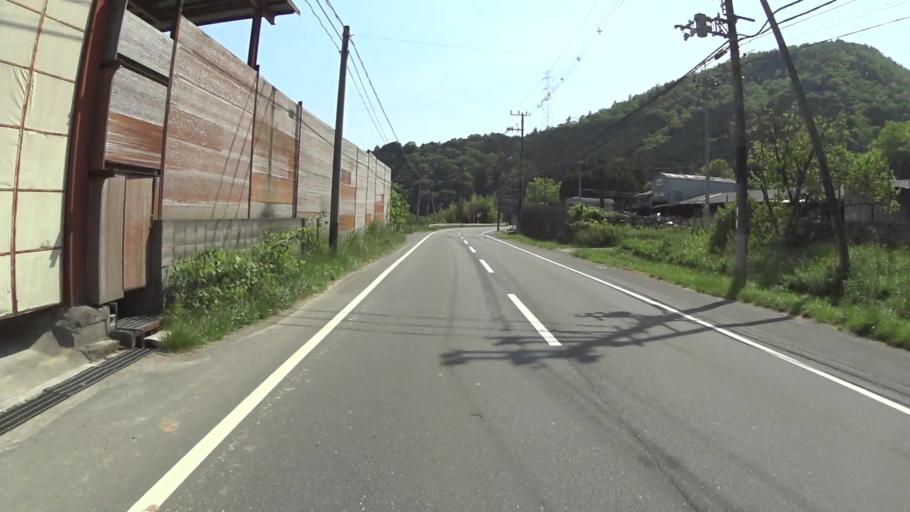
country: JP
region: Kyoto
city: Kameoka
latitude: 35.1423
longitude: 135.4958
